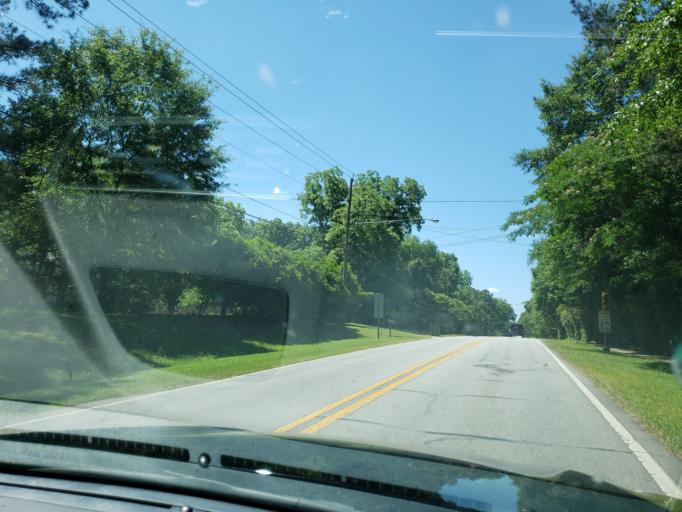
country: US
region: Alabama
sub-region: Lee County
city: Auburn
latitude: 32.6260
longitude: -85.4819
